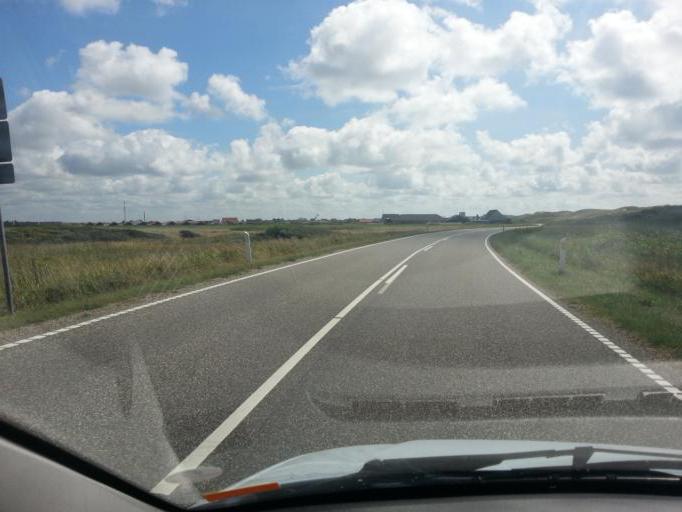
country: DK
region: Central Jutland
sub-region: Holstebro Kommune
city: Ulfborg
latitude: 56.3818
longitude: 8.1220
